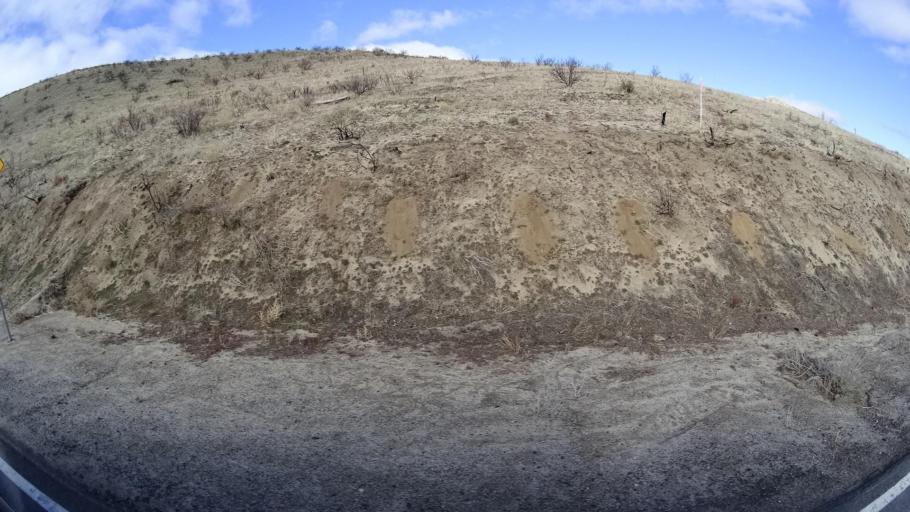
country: US
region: Nevada
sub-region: Washoe County
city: Cold Springs
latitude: 39.8433
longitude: -119.9353
